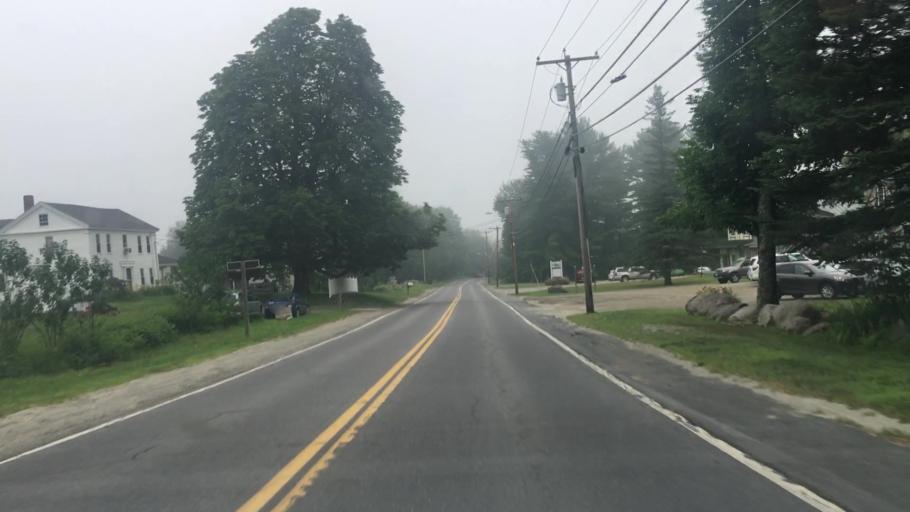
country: US
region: Maine
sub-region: Kennebec County
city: Oakland
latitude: 44.5335
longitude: -69.7234
